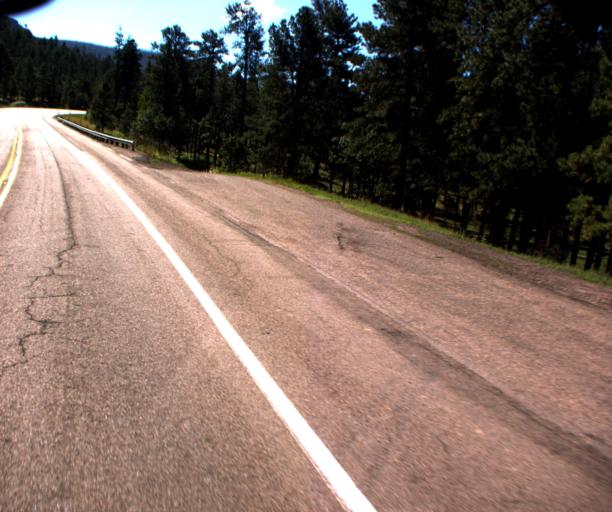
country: US
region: Arizona
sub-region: Apache County
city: Eagar
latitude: 33.9048
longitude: -109.1637
